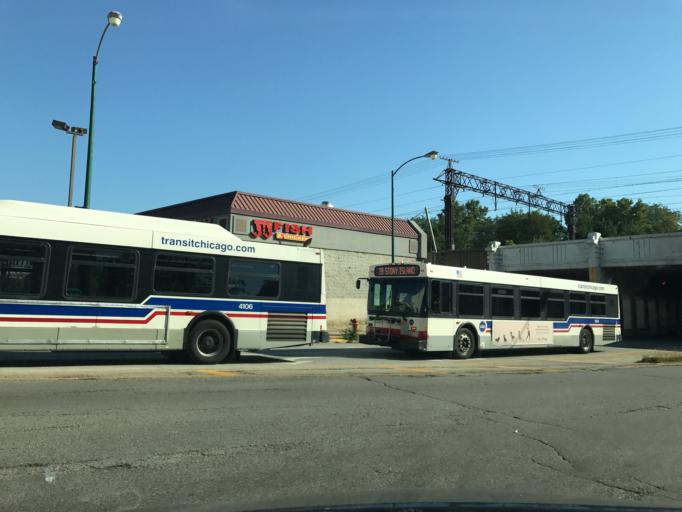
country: US
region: Illinois
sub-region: Cook County
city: Chicago
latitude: 41.8095
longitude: -87.5921
